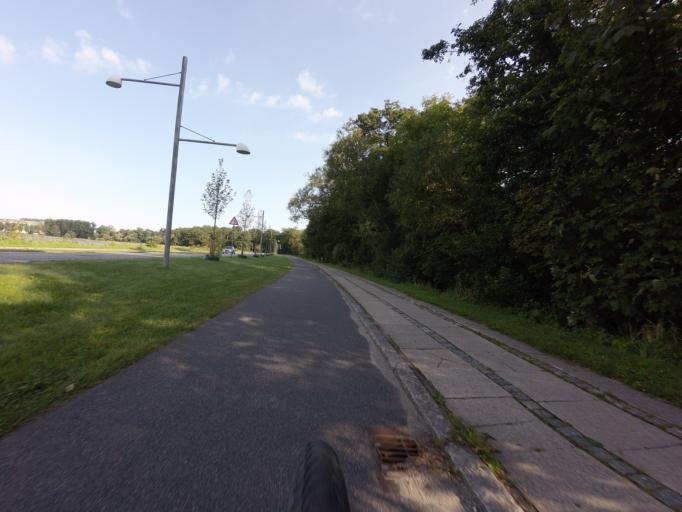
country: DK
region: Zealand
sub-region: Soro Kommune
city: Frederiksberg
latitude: 55.4260
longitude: 11.5657
